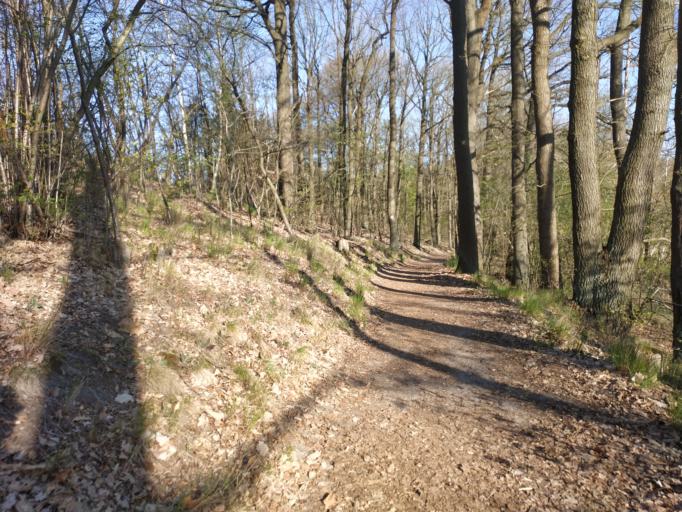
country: DE
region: Brandenburg
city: Strausberg
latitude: 52.5664
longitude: 13.8347
